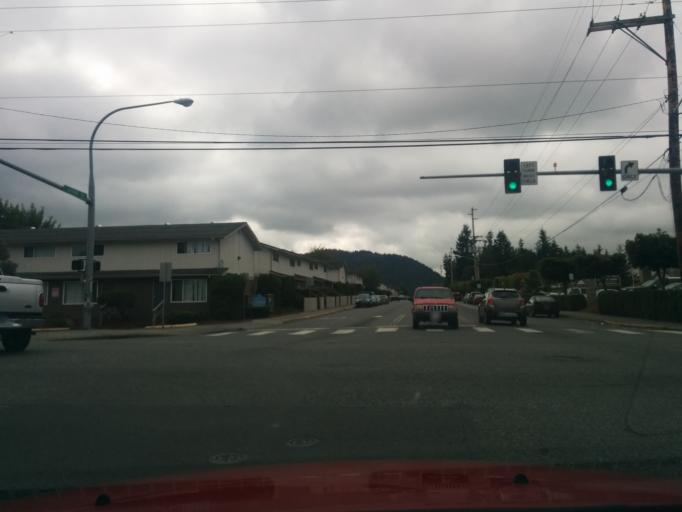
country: US
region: Washington
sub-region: Skagit County
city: Mount Vernon
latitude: 48.4213
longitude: -122.3134
